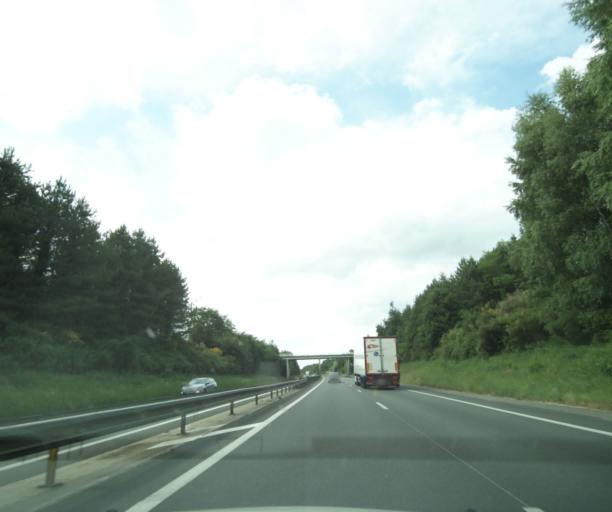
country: FR
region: Centre
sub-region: Departement du Cher
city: Vierzon
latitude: 47.2219
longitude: 2.1095
